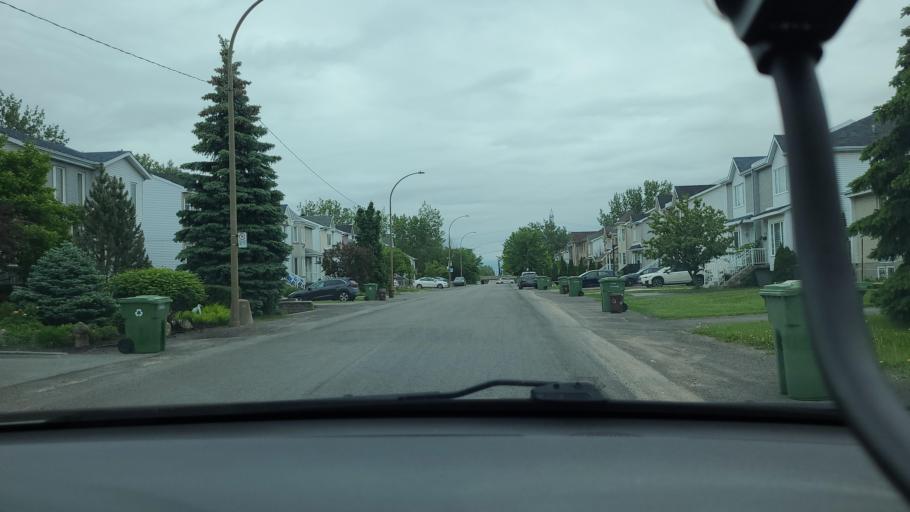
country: CA
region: Quebec
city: Montreal-Est
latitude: 45.6673
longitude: -73.5371
